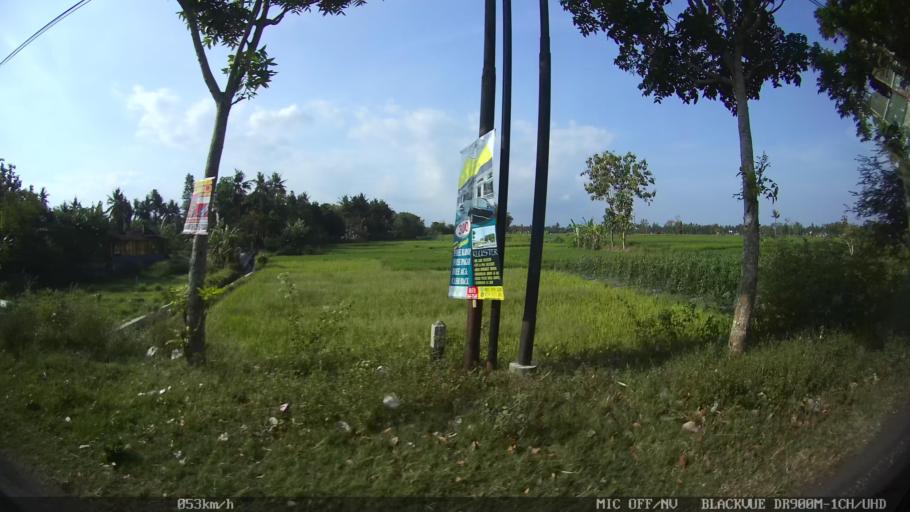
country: ID
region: Daerah Istimewa Yogyakarta
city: Pandak
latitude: -7.9019
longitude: 110.3041
